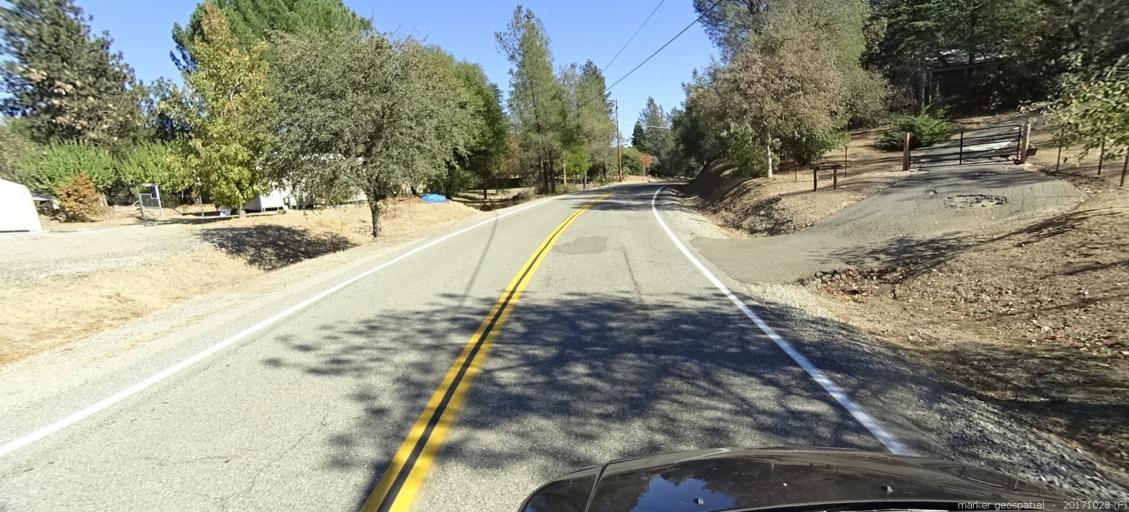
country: US
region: California
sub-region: Shasta County
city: Shasta
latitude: 40.6169
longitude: -122.4876
